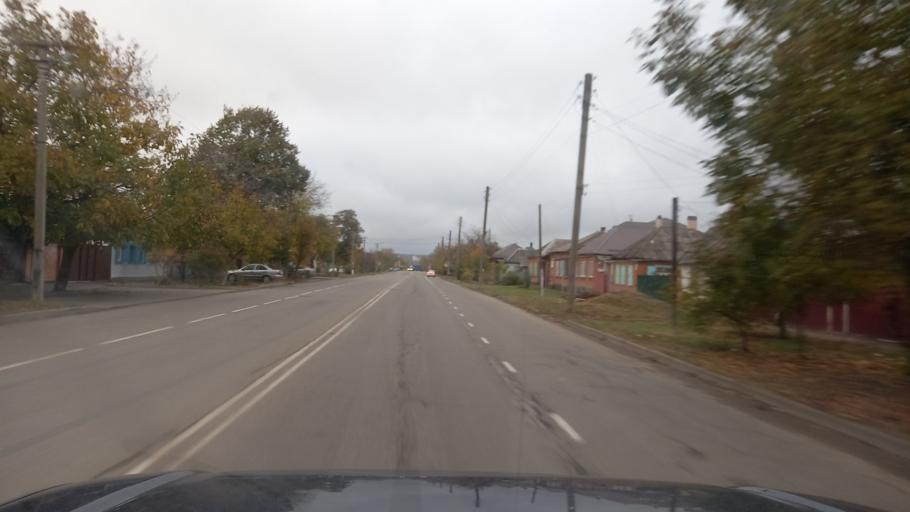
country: RU
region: Adygeya
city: Maykop
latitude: 44.6115
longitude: 40.1150
